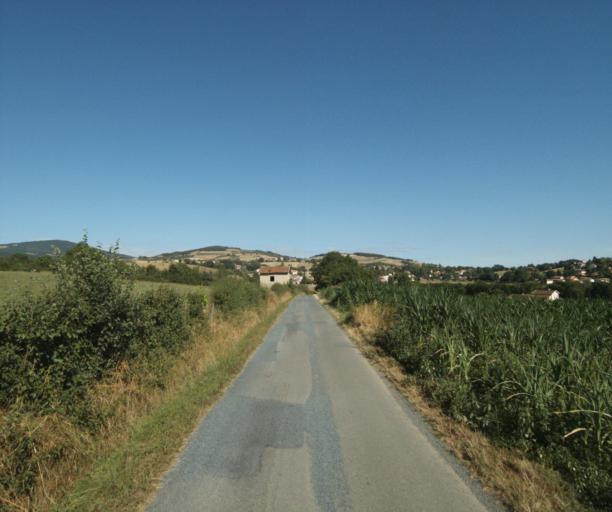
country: FR
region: Rhone-Alpes
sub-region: Departement du Rhone
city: Savigny
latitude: 45.8100
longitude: 4.5822
